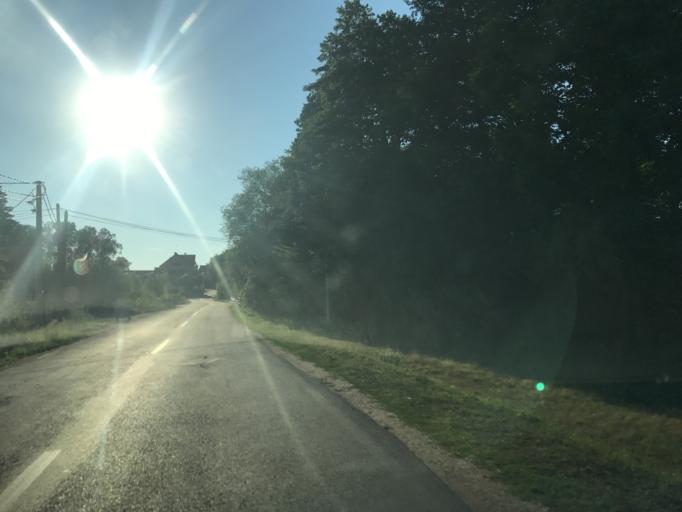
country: RO
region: Mehedinti
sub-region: Comuna Gogosu
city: Ostrovu Mare
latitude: 44.2897
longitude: 22.3561
